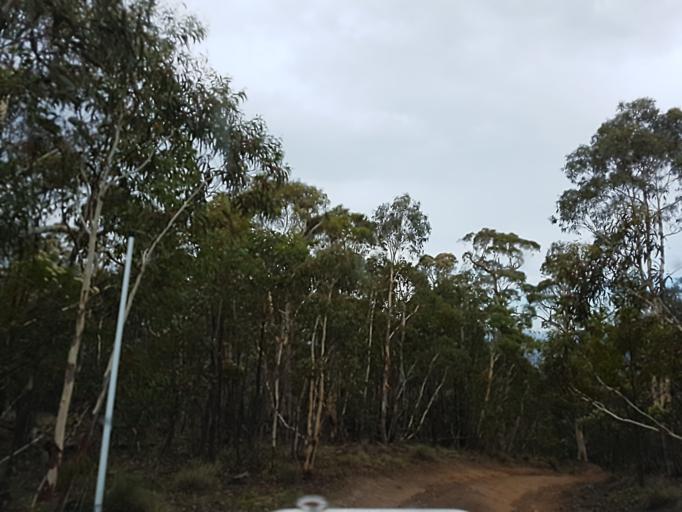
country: AU
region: New South Wales
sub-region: Snowy River
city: Jindabyne
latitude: -36.9023
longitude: 148.3422
